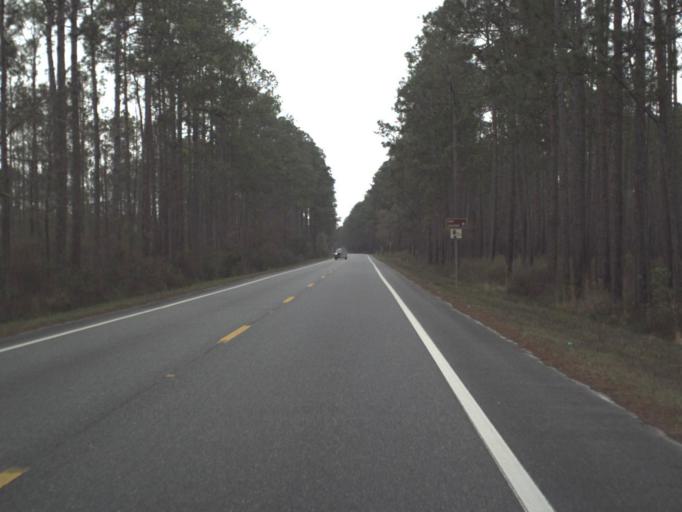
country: US
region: Florida
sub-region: Franklin County
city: Apalachicola
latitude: 29.9661
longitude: -84.9757
